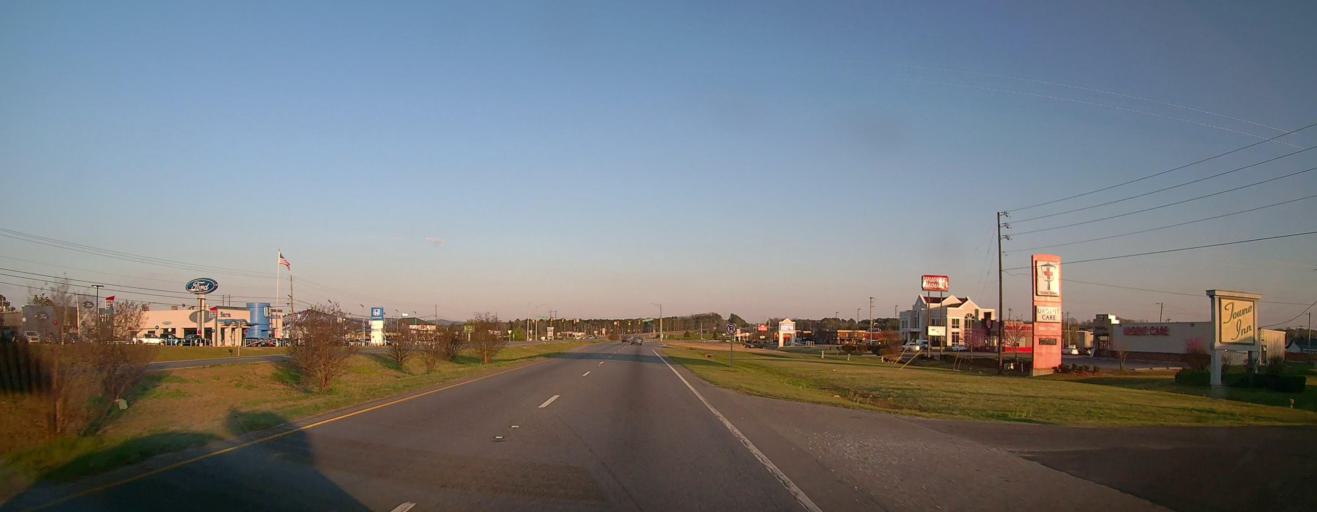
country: US
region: Alabama
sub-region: Talladega County
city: Mignon
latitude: 33.1765
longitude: -86.2924
